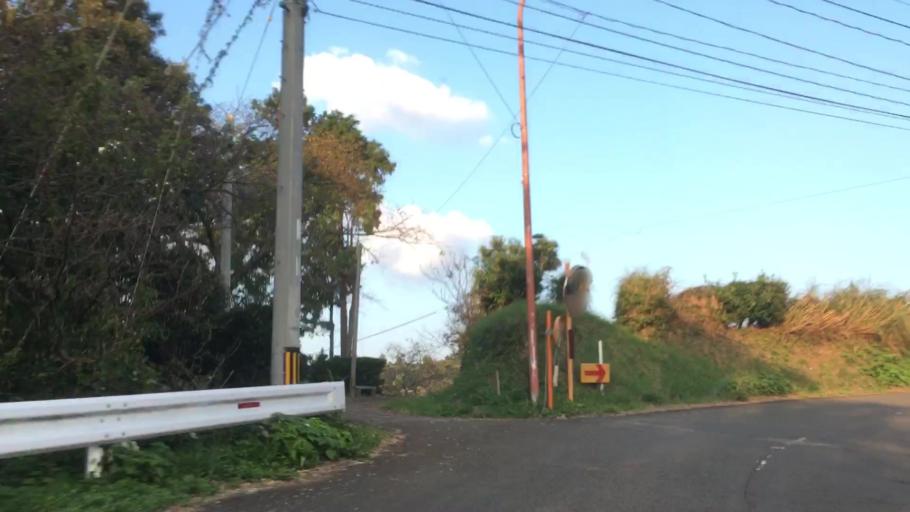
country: JP
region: Nagasaki
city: Sasebo
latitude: 33.0366
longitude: 129.6648
